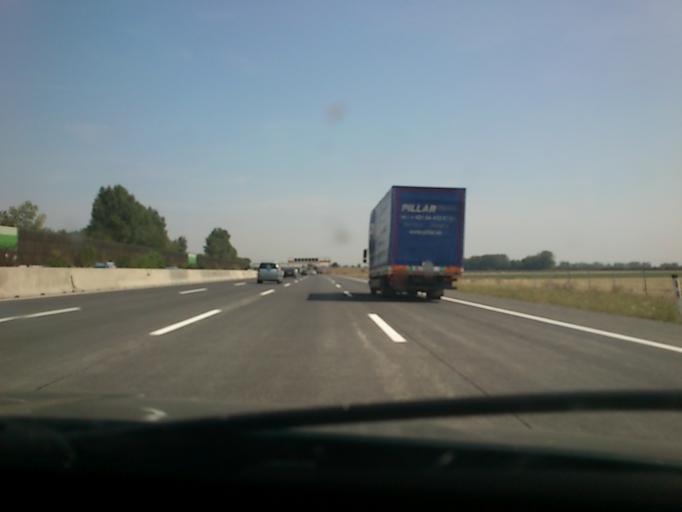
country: AT
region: Lower Austria
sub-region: Politischer Bezirk Baden
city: Traiskirchen
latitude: 48.0141
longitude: 16.3211
